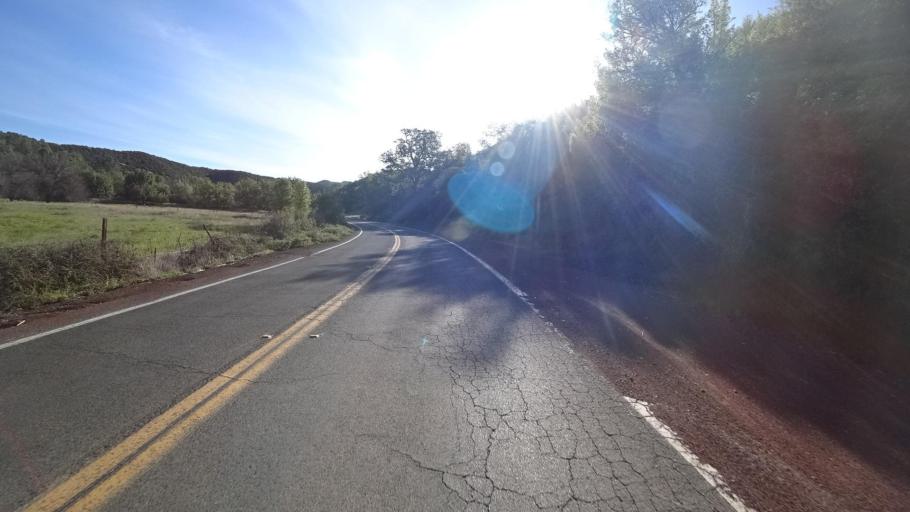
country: US
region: California
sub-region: Lake County
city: North Lakeport
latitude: 39.0913
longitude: -122.9562
